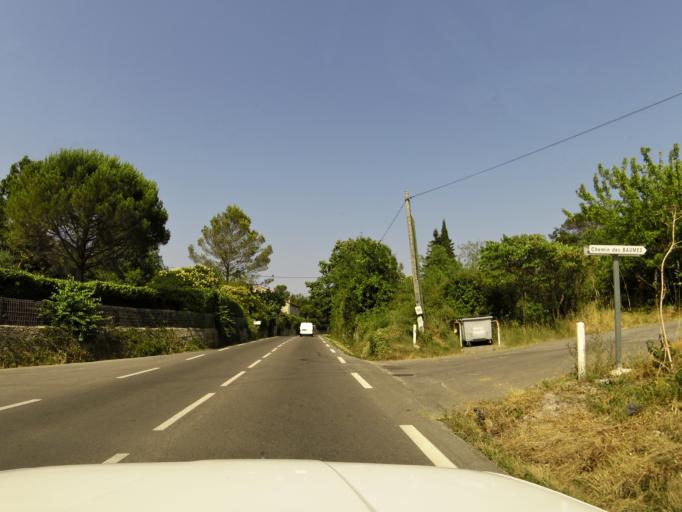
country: FR
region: Languedoc-Roussillon
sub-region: Departement du Gard
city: Anduze
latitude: 44.0554
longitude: 3.9960
